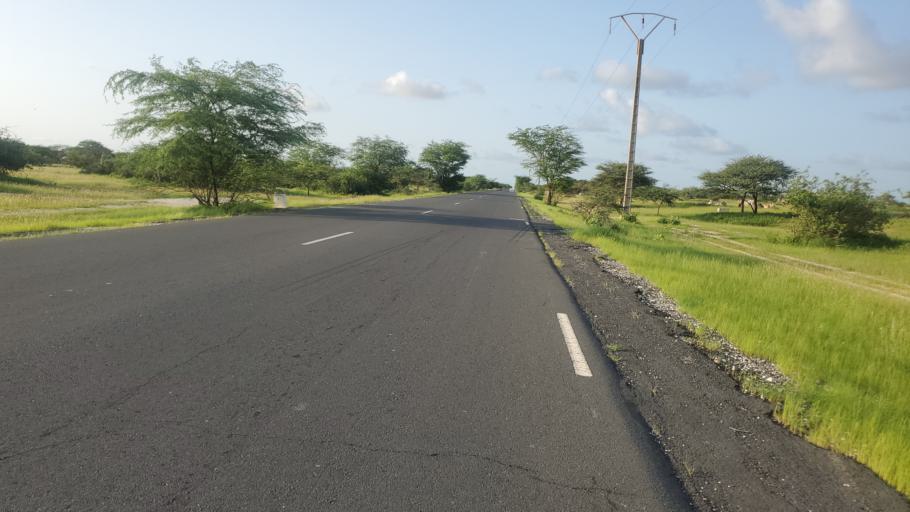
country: SN
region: Saint-Louis
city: Saint-Louis
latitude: 16.1712
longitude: -16.4097
